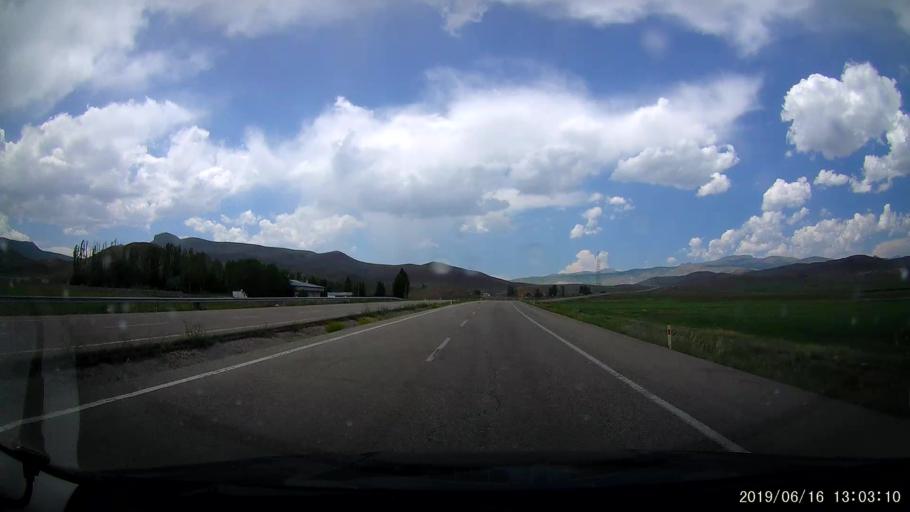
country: TR
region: Agri
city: Sulucem
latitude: 39.5790
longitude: 43.7963
